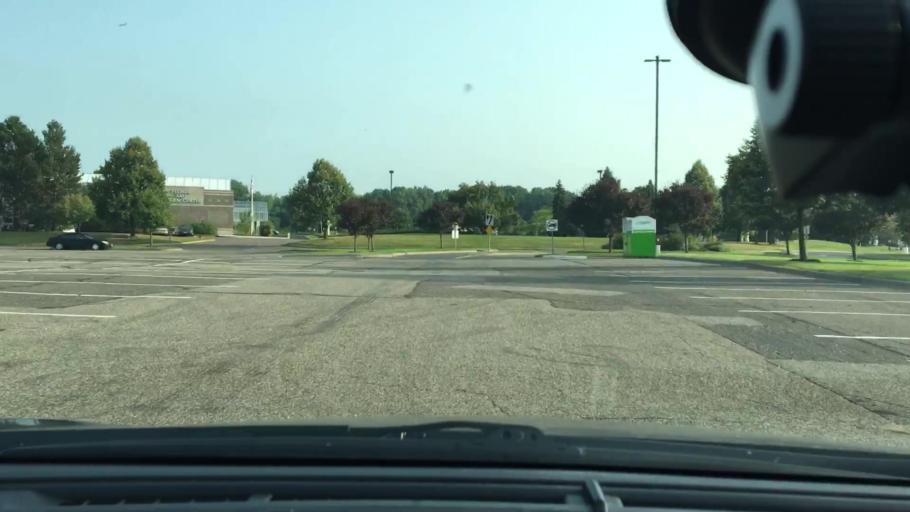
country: US
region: Minnesota
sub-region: Hennepin County
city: Plymouth
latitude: 44.9862
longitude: -93.4087
